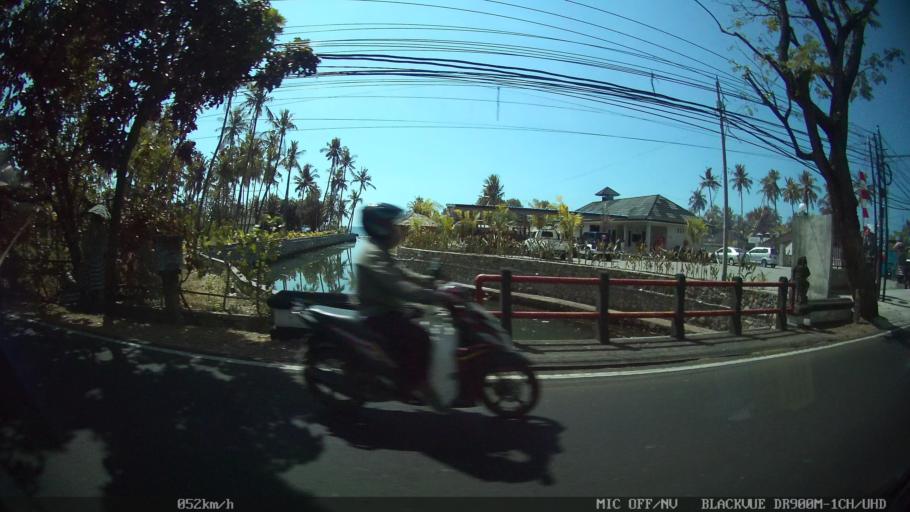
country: ID
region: Bali
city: Pegayaman
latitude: -8.1759
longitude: 115.0034
